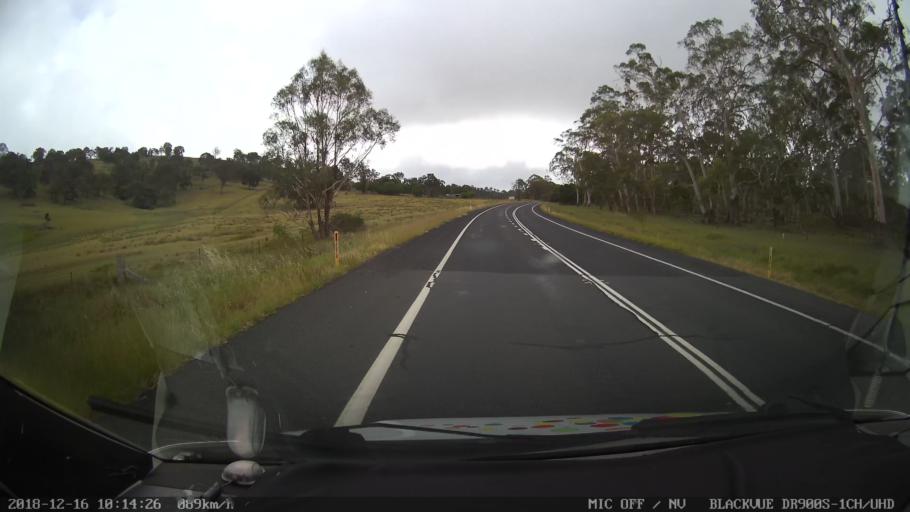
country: AU
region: New South Wales
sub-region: Tenterfield Municipality
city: Carrolls Creek
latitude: -29.2867
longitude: 151.9627
